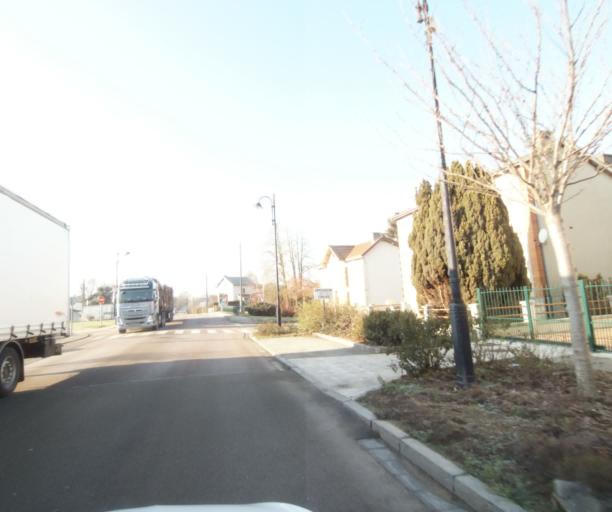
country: FR
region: Champagne-Ardenne
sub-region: Departement de la Haute-Marne
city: Montier-en-Der
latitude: 48.4747
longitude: 4.7672
